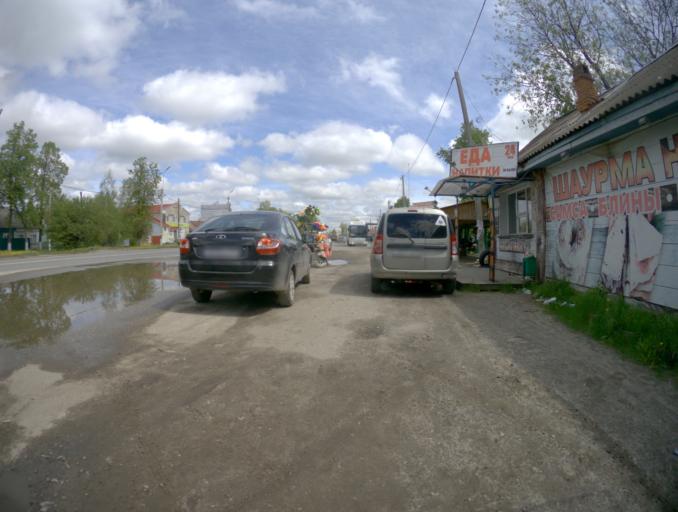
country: RU
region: Rjazan
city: Tuma
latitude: 55.1457
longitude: 40.5467
